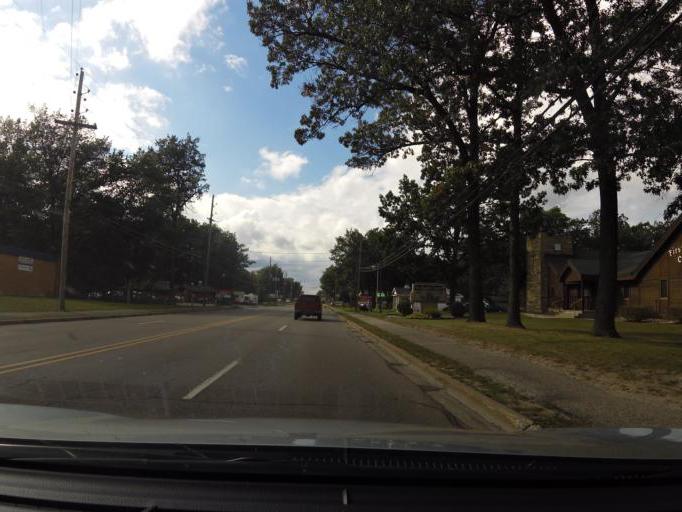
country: US
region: Michigan
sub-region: Roscommon County
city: Prudenville
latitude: 44.2986
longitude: -84.6677
